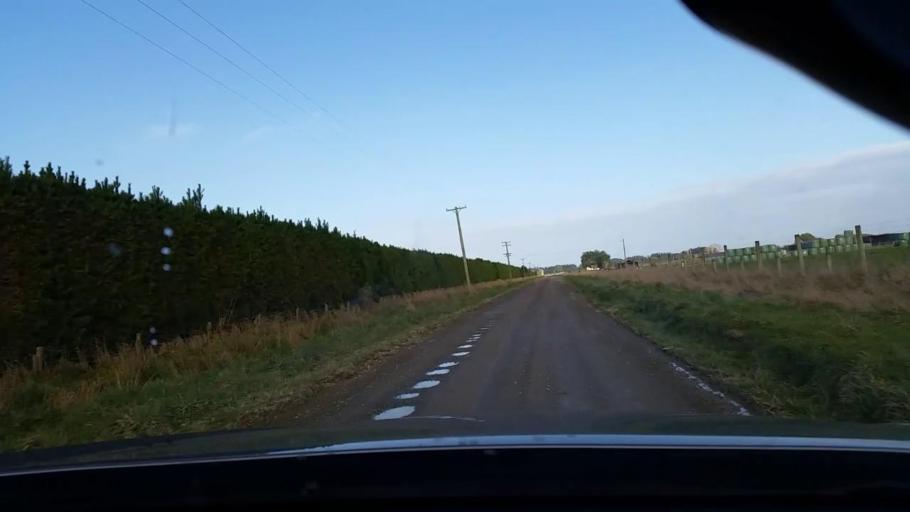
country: NZ
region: Southland
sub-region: Invercargill City
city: Invercargill
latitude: -46.2830
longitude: 168.2946
